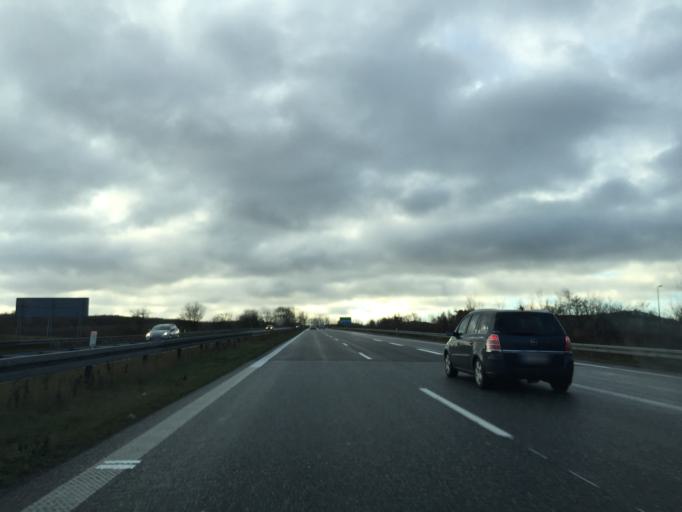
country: DK
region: Zealand
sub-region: Slagelse Kommune
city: Slagelse
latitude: 55.4152
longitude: 11.4122
